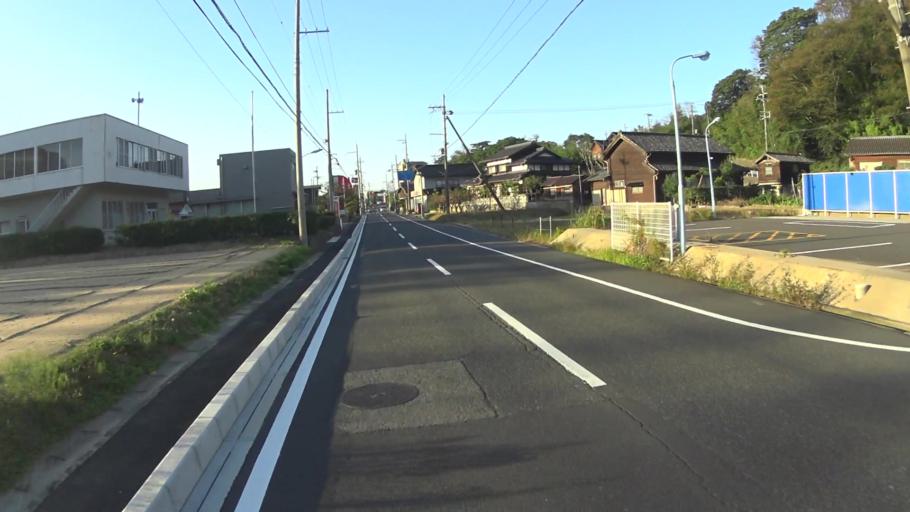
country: JP
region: Hyogo
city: Toyooka
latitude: 35.6554
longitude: 134.9688
